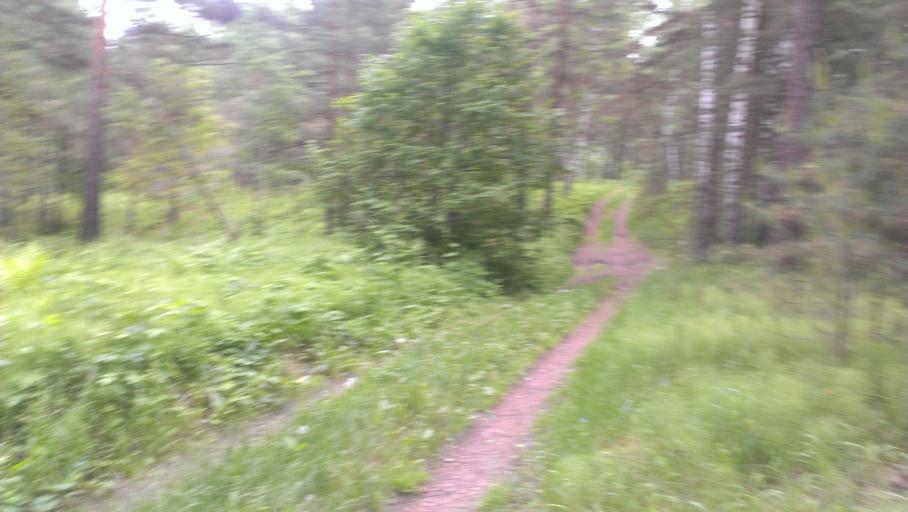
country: RU
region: Altai Krai
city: Sannikovo
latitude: 53.3430
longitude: 84.0452
